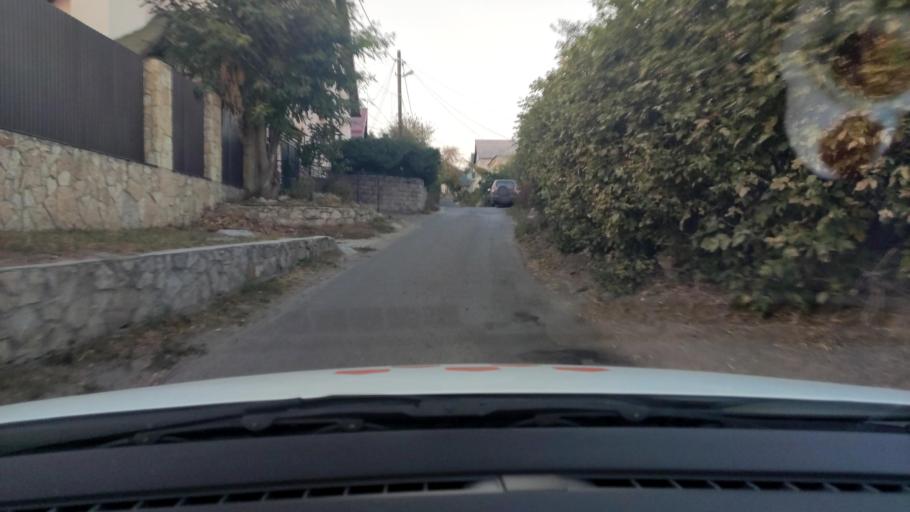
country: RU
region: Voronezj
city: Voronezh
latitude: 51.6870
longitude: 39.2244
